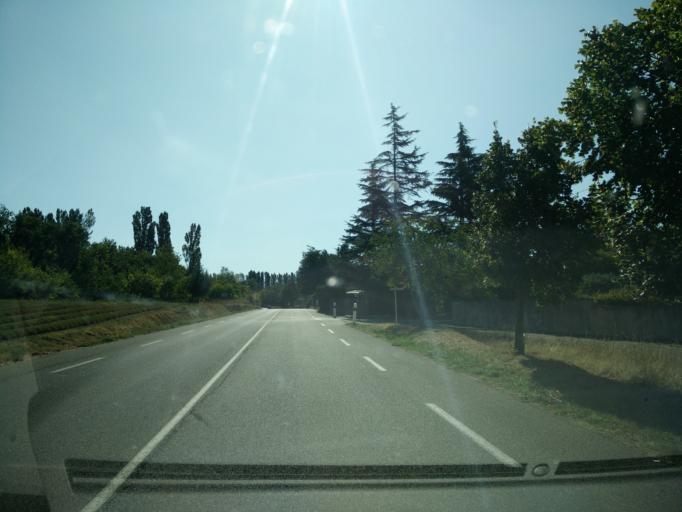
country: FR
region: Rhone-Alpes
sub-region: Departement de la Drome
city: Dieulefit
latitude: 44.5323
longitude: 5.0011
